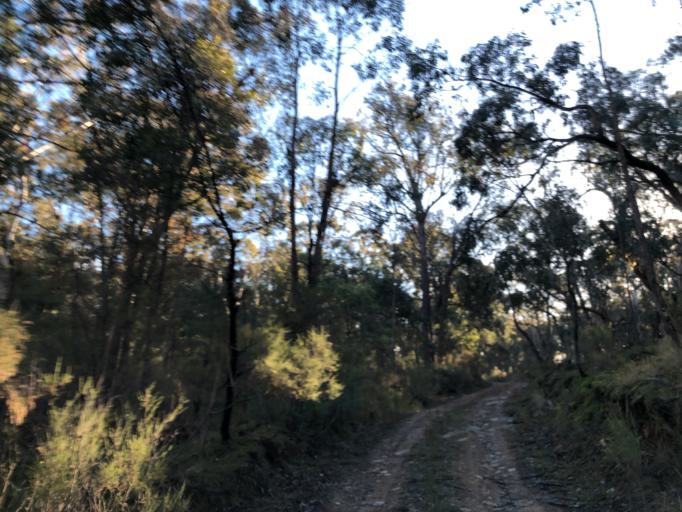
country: AU
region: Victoria
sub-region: Mount Alexander
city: Castlemaine
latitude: -37.2316
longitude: 144.2781
